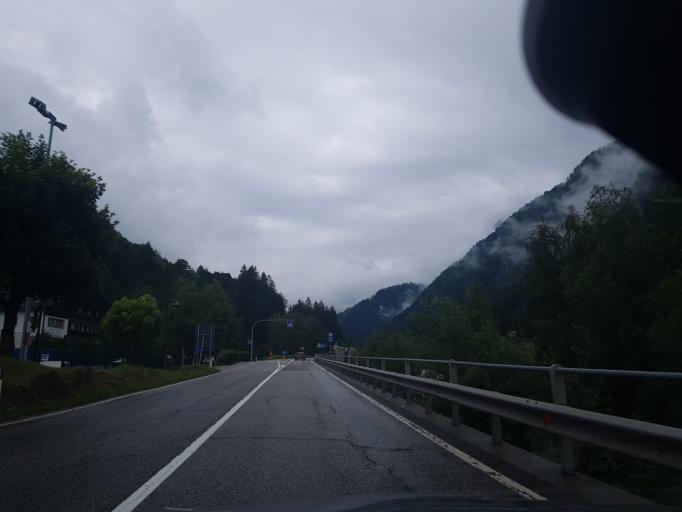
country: IT
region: Trentino-Alto Adige
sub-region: Bolzano
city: Ortisei
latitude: 46.5692
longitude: 11.6820
